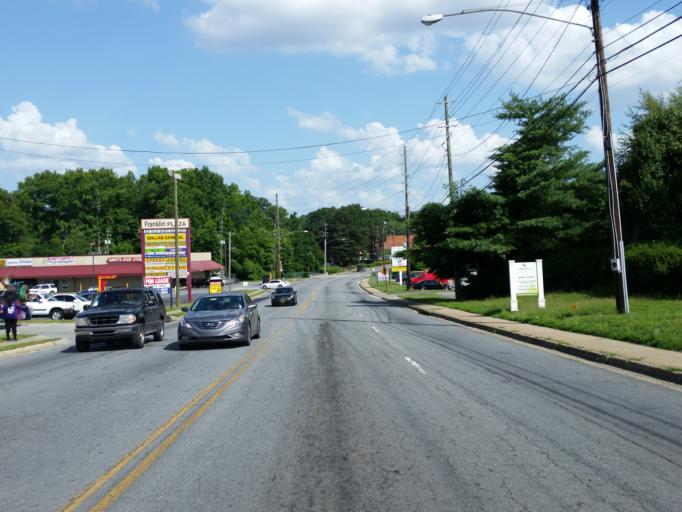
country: US
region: Georgia
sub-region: Cobb County
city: Smyrna
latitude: 33.9285
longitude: -84.4942
